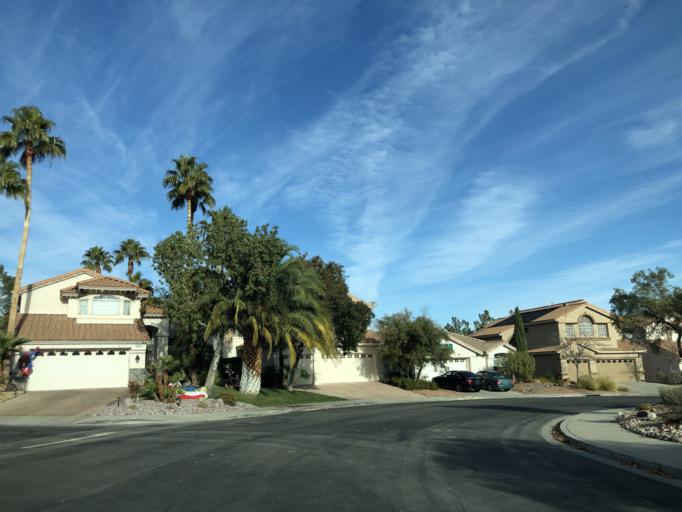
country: US
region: Nevada
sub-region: Clark County
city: Whitney
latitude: 36.0225
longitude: -115.0700
